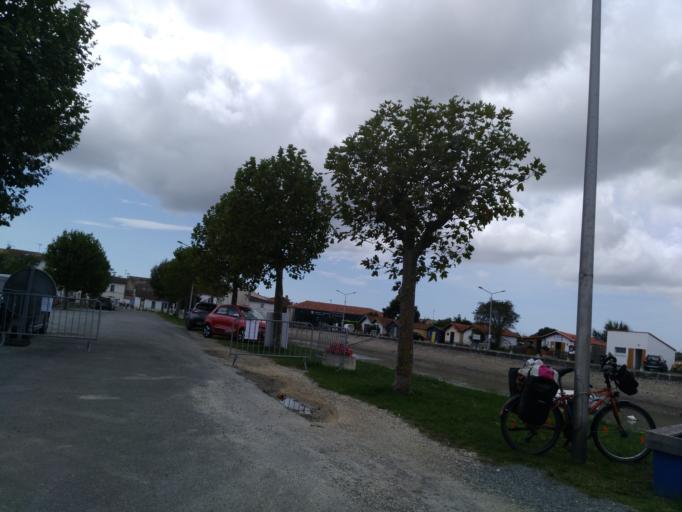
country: FR
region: Poitou-Charentes
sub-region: Departement de la Charente-Maritime
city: Le Gua
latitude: 45.7097
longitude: -0.9761
